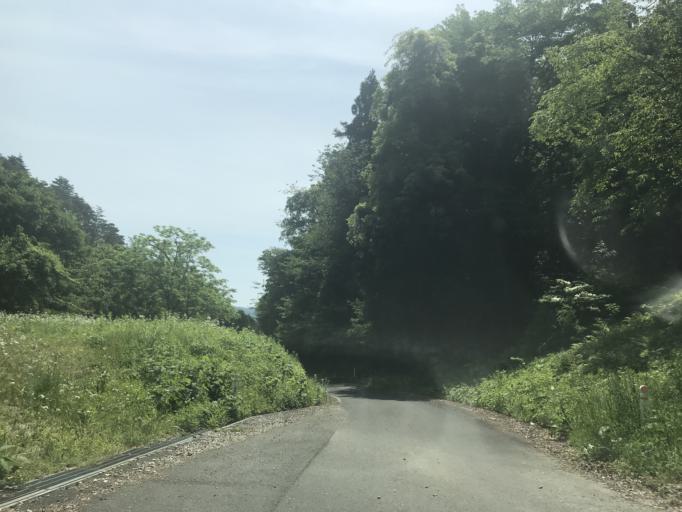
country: JP
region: Iwate
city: Ichinoseki
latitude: 38.9693
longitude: 141.2281
